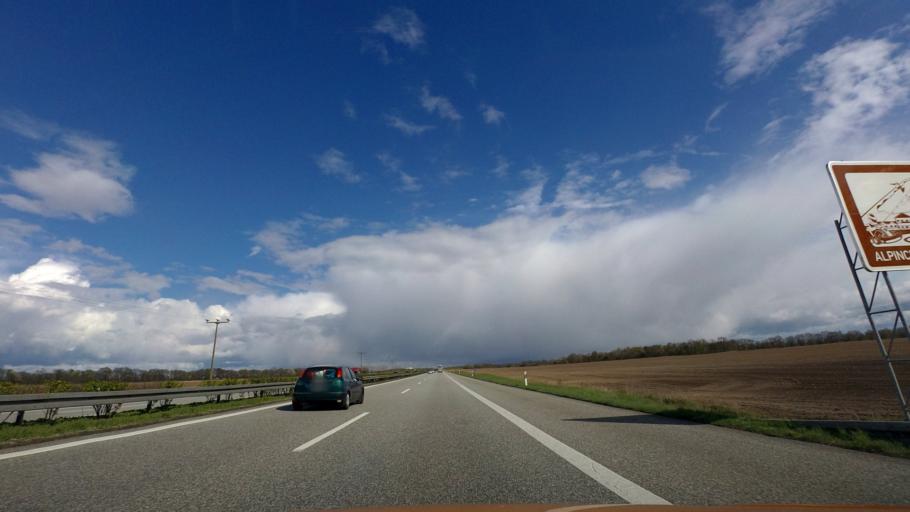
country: DE
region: Mecklenburg-Vorpommern
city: Wittenburg
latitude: 53.5039
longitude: 11.0279
